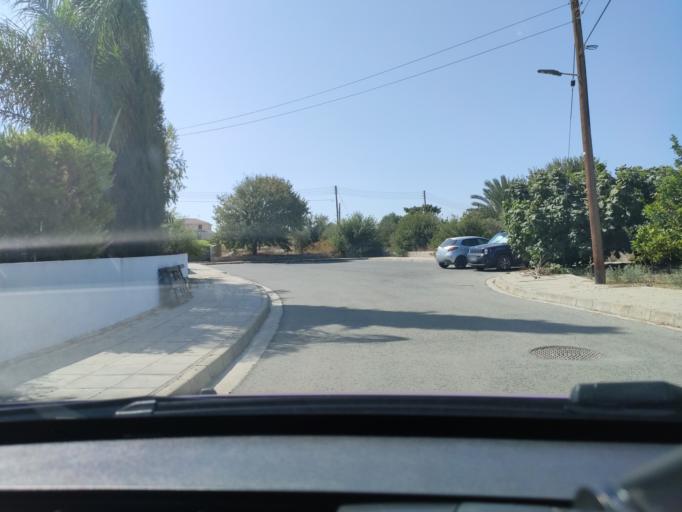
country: CY
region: Lefkosia
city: Geri
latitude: 35.1177
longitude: 33.3671
